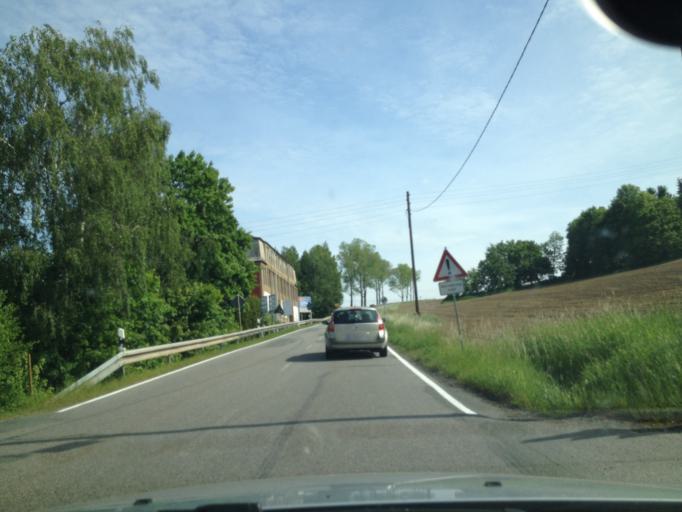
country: DE
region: Saxony
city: Burkhardtsdorf
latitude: 50.7400
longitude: 12.9249
